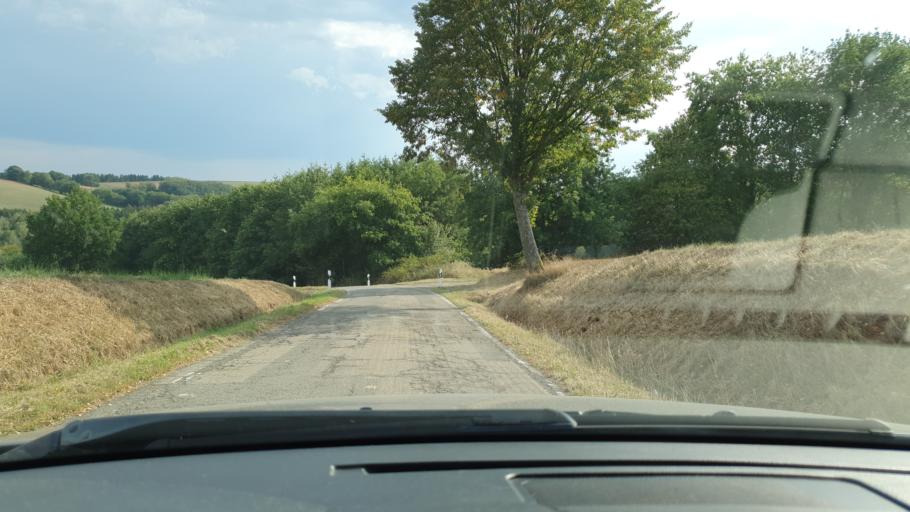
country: DE
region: Rheinland-Pfalz
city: Gerhardsbrunn
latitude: 49.3474
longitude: 7.5282
